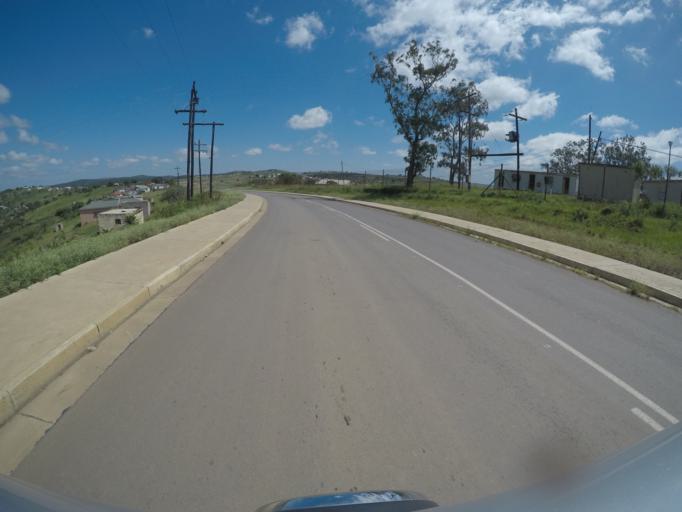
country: ZA
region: KwaZulu-Natal
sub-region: uThungulu District Municipality
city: Empangeni
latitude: -28.6054
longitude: 31.7431
